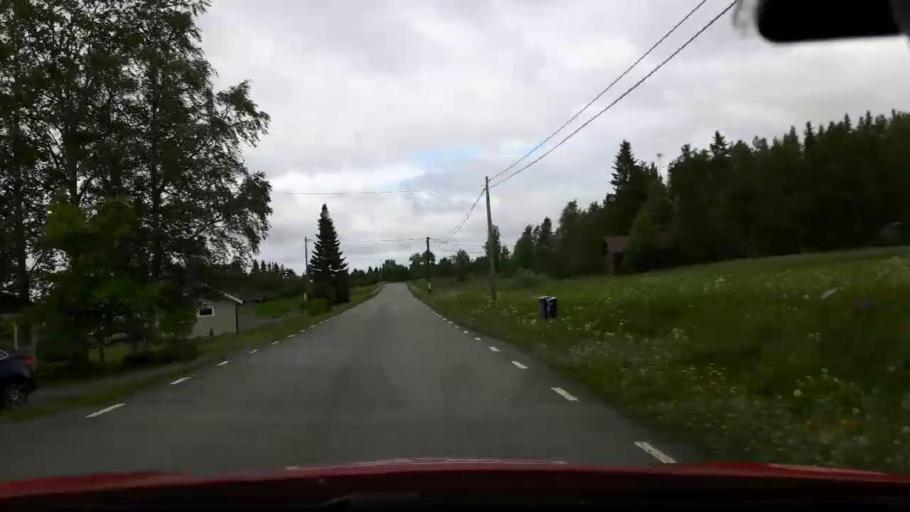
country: SE
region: Jaemtland
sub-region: Krokoms Kommun
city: Krokom
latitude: 63.2608
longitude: 14.5377
